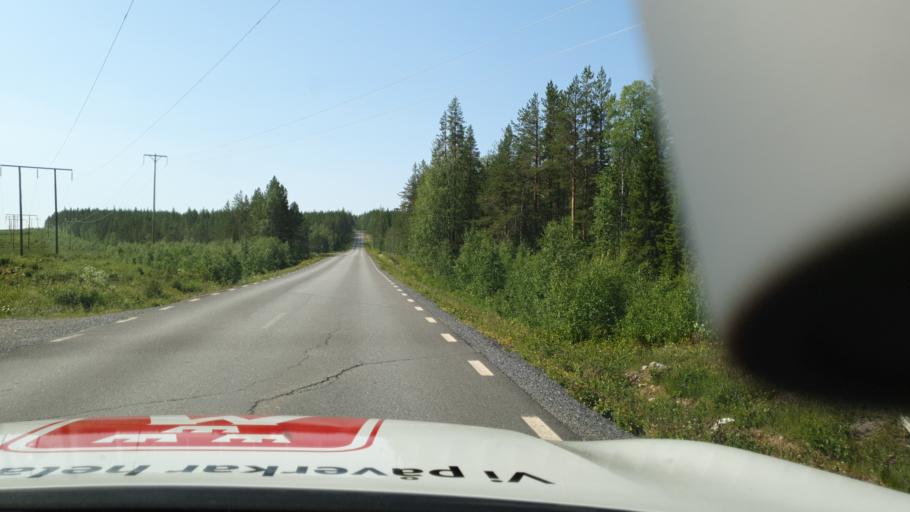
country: SE
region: Vaesterbotten
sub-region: Skelleftea Kommun
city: Langsele
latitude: 64.9803
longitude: 20.0639
